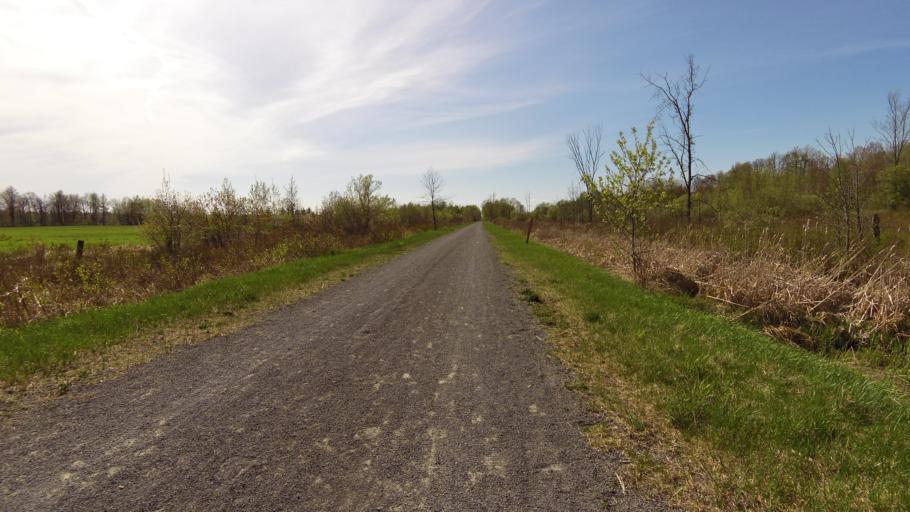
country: CA
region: Ontario
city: Clarence-Rockland
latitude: 45.4184
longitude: -75.4686
